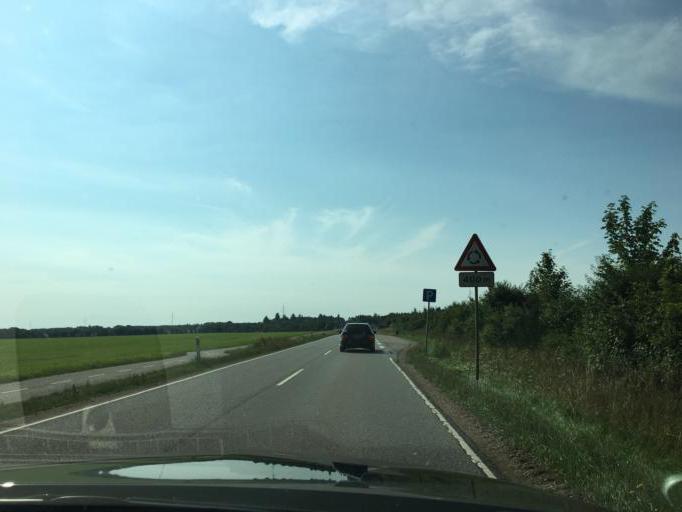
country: DK
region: South Denmark
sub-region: Varde Kommune
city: Varde
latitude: 55.6341
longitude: 8.4251
